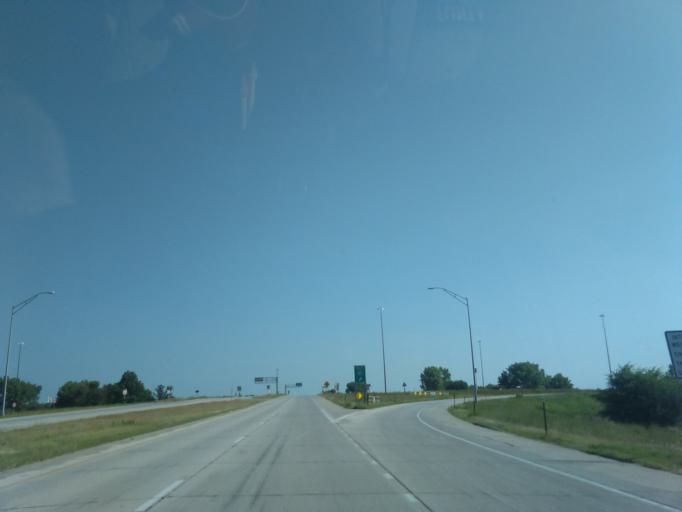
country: US
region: Nebraska
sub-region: Hall County
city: Grand Island
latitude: 40.8234
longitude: -98.3786
